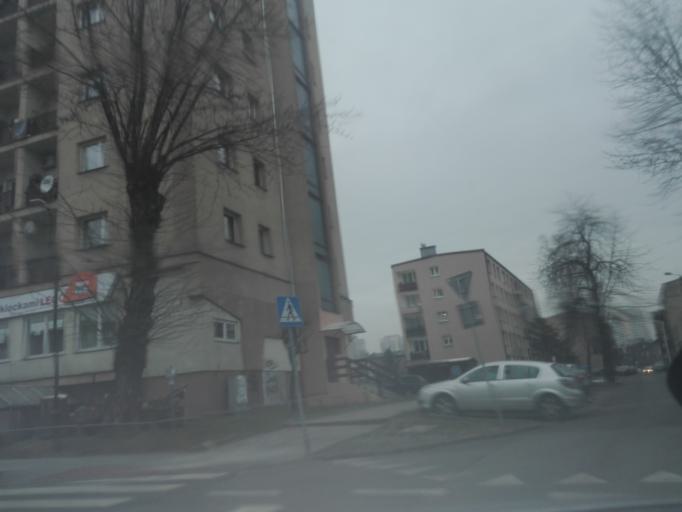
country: PL
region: Silesian Voivodeship
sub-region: Katowice
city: Katowice
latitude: 50.2550
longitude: 19.0396
